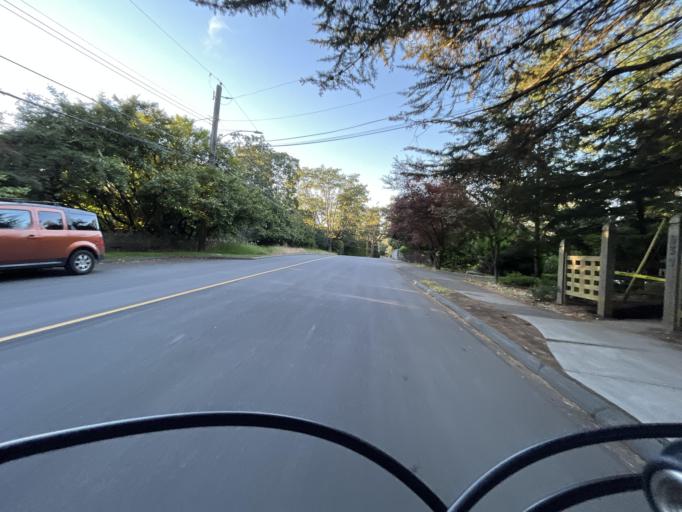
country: CA
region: British Columbia
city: Oak Bay
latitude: 48.4226
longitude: -123.3223
